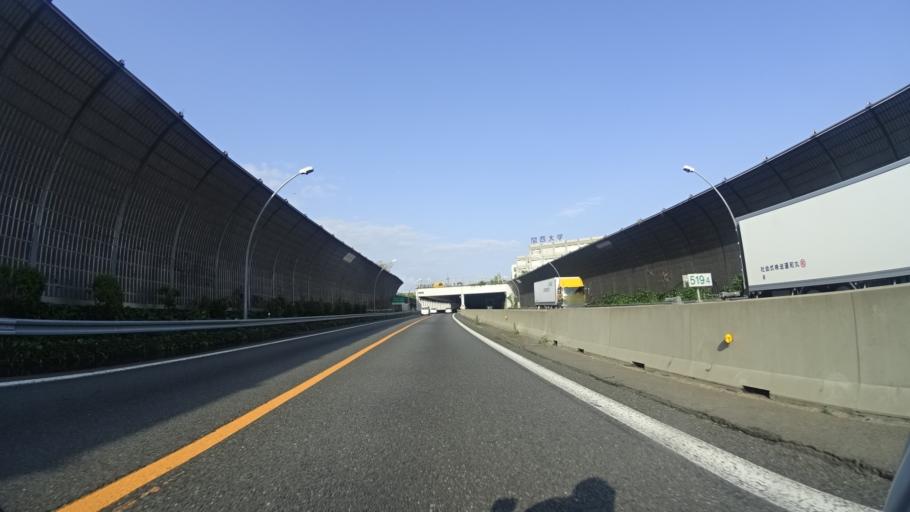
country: JP
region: Osaka
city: Suita
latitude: 34.7729
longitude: 135.5145
